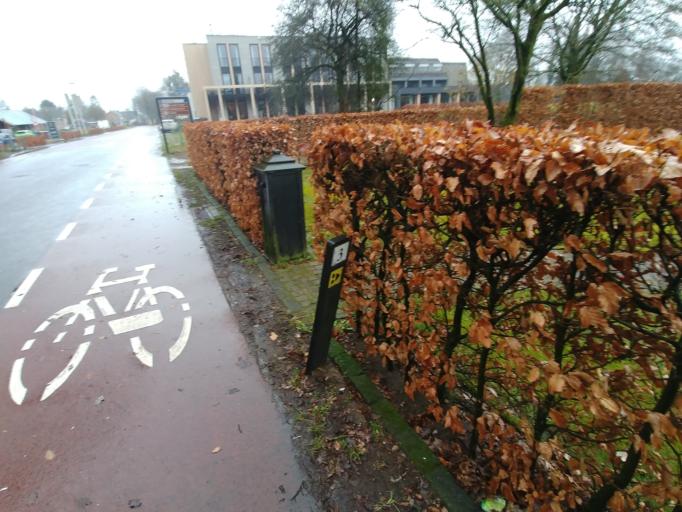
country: NL
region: Gelderland
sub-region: Gemeente Ede
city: Otterlo
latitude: 52.1023
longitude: 5.7796
